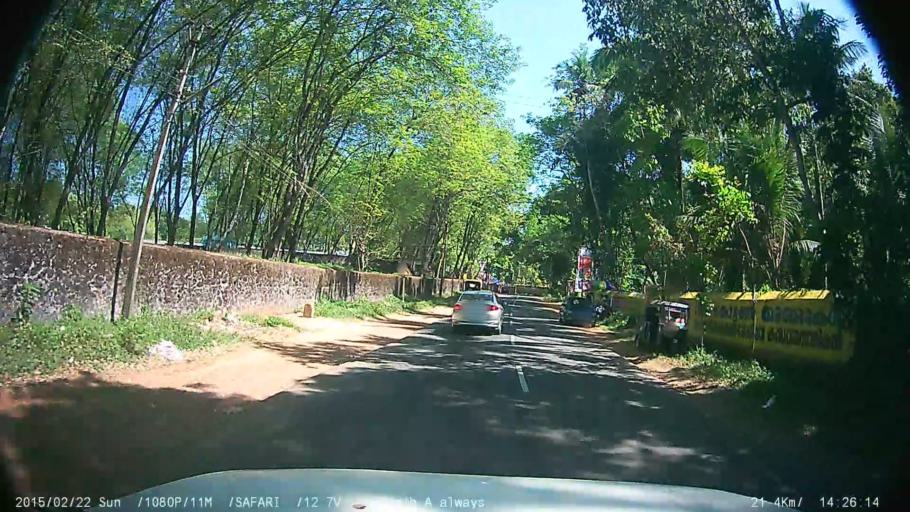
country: IN
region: Kerala
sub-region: Kottayam
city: Erattupetta
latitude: 9.5687
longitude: 76.7260
